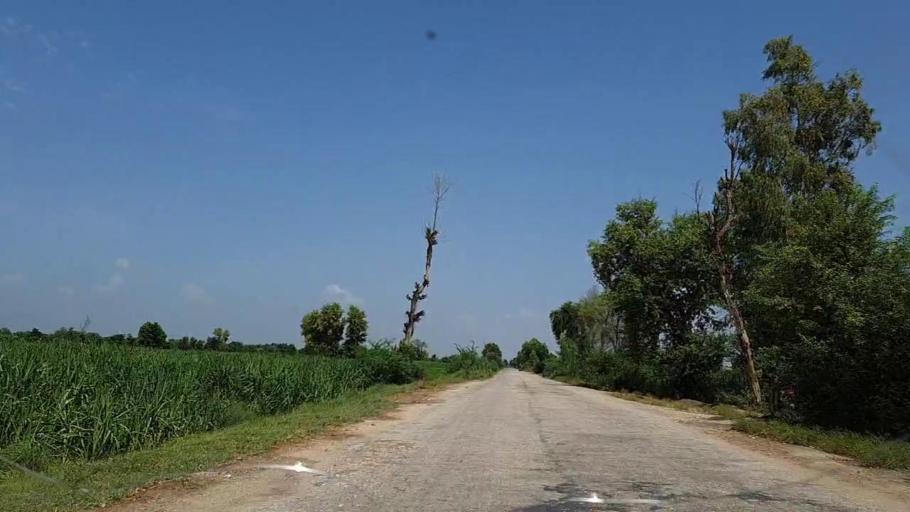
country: PK
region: Sindh
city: Pad Idan
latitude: 26.8054
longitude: 68.2121
